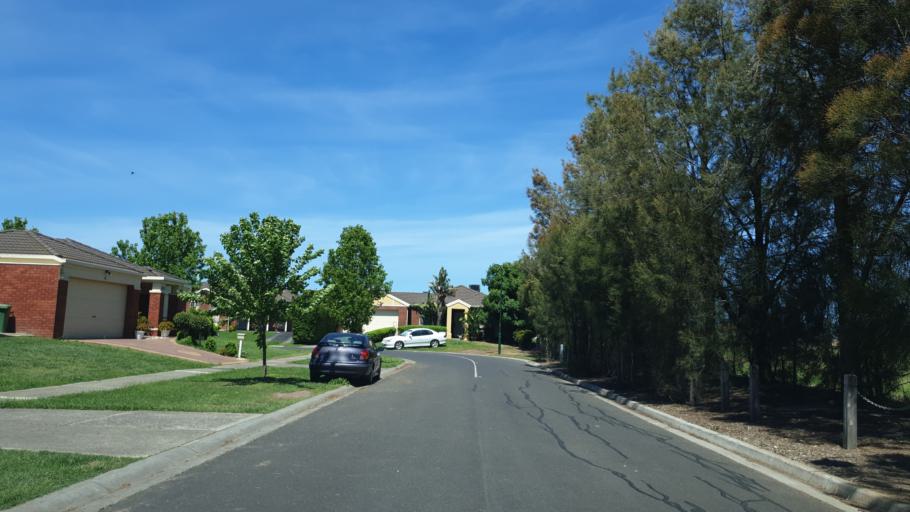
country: AU
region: Victoria
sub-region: Casey
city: Narre Warren South
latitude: -38.0582
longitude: 145.2828
